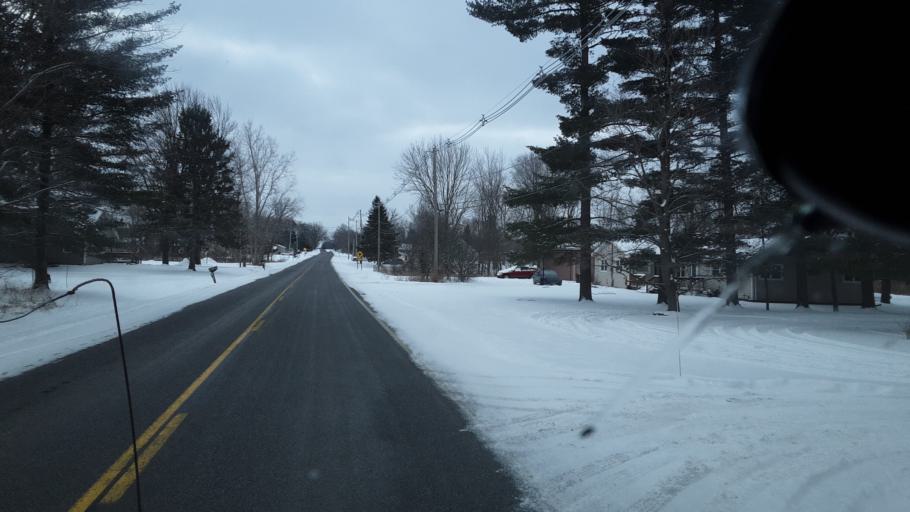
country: US
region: Michigan
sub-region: Ingham County
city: Holt
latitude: 42.5993
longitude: -84.5428
